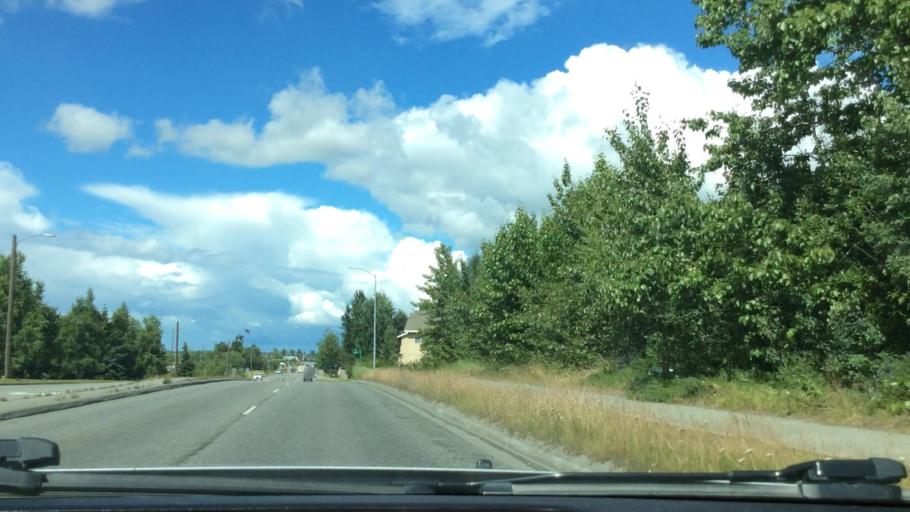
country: US
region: Alaska
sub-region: Anchorage Municipality
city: Anchorage
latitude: 61.2119
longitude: -149.8081
